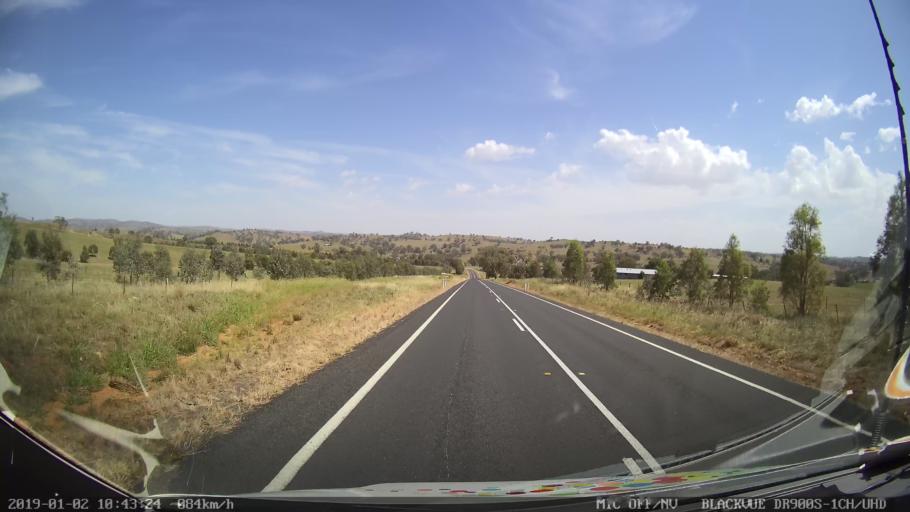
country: AU
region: New South Wales
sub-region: Cootamundra
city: Cootamundra
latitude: -34.7729
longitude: 148.3043
